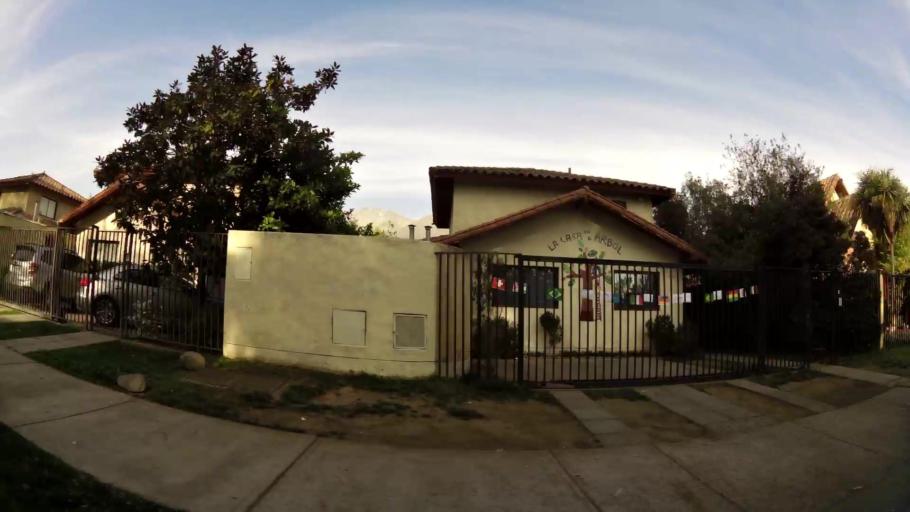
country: CL
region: Santiago Metropolitan
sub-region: Provincia de Santiago
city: Villa Presidente Frei, Nunoa, Santiago, Chile
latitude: -33.5056
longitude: -70.5535
